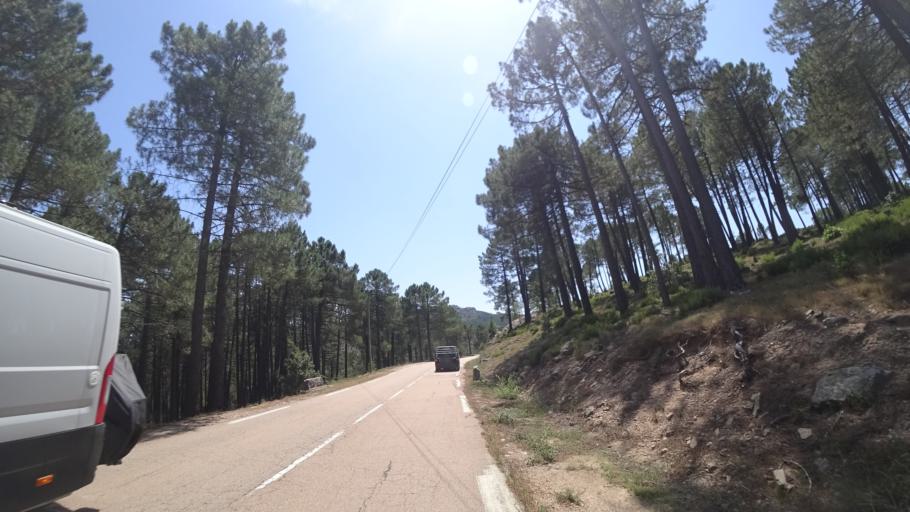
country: FR
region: Corsica
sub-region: Departement de la Corse-du-Sud
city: Zonza
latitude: 41.6724
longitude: 9.2079
